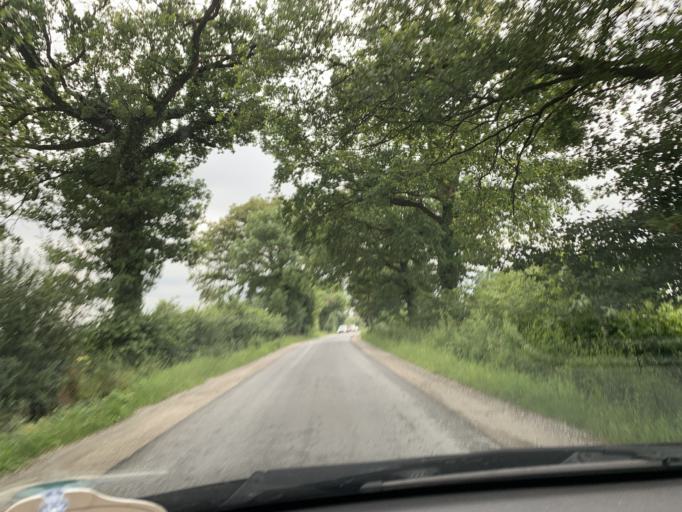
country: DE
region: North Rhine-Westphalia
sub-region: Regierungsbezirk Munster
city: Ennigerloh
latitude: 51.8348
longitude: 8.0750
